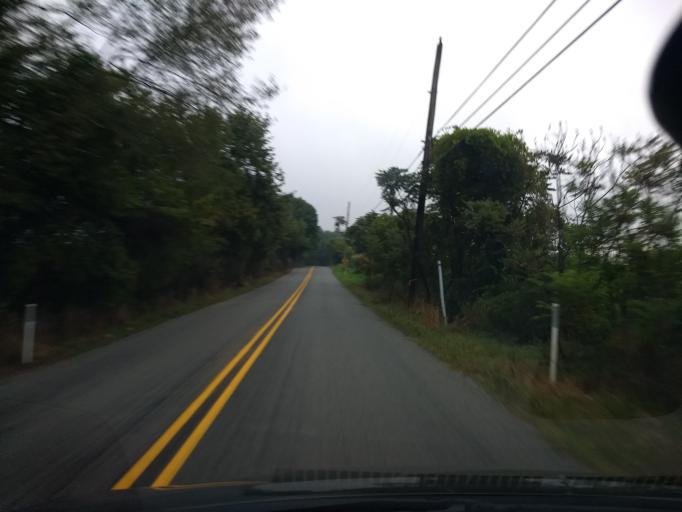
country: US
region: Pennsylvania
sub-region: Westmoreland County
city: Greensburg
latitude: 40.3450
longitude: -79.5052
